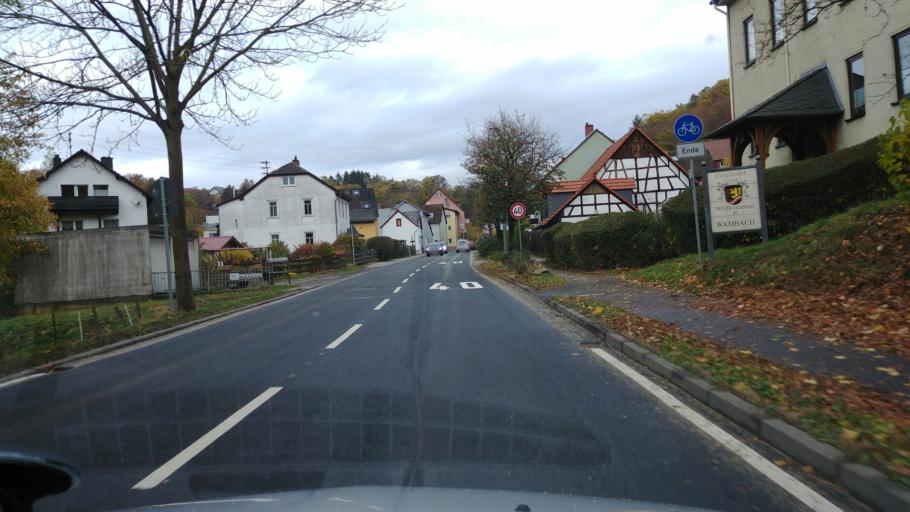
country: DE
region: Hesse
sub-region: Regierungsbezirk Darmstadt
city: Schlangenbad
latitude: 50.1074
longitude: 8.0996
